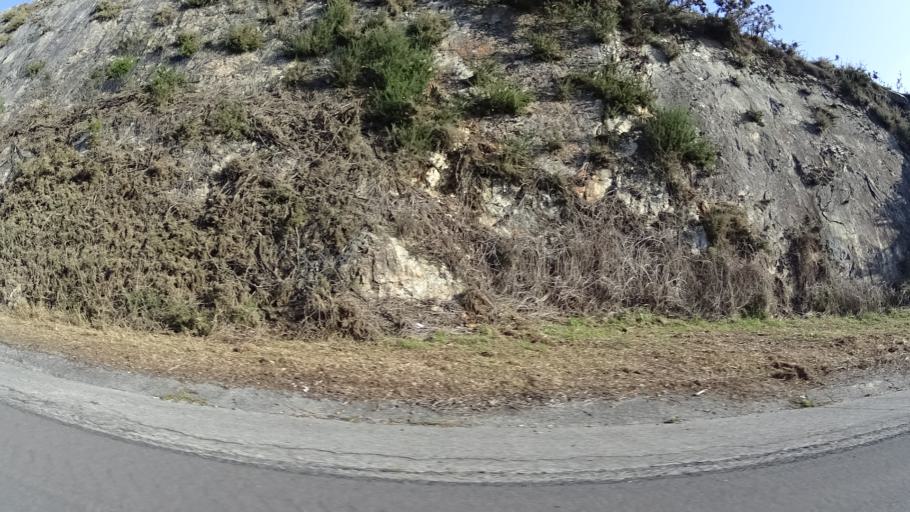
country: ES
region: Galicia
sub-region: Provincia da Coruna
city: Aranga
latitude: 43.2328
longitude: -8.0682
